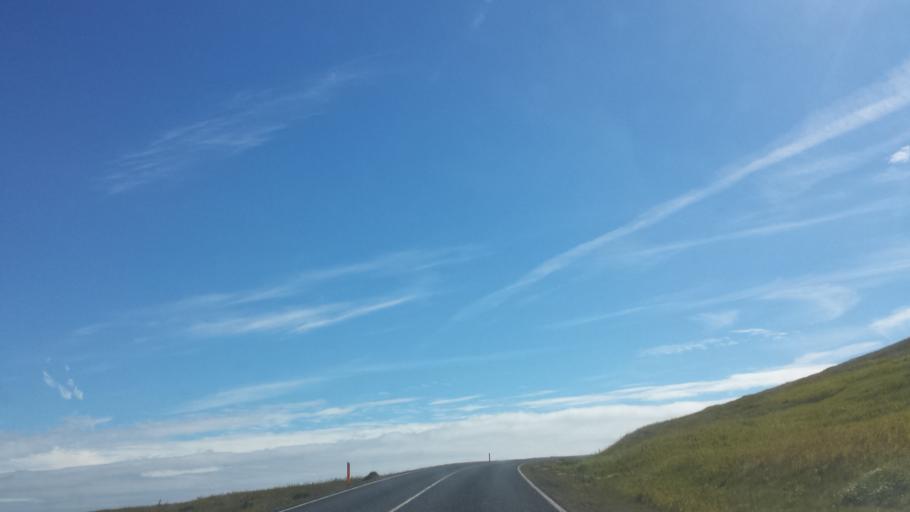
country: IS
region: South
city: Vestmannaeyjar
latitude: 63.4312
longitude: -20.2568
